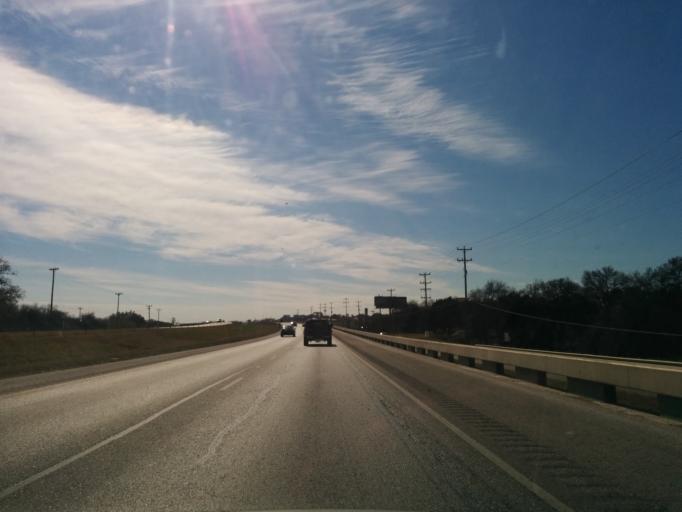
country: US
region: Texas
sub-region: Bexar County
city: Cross Mountain
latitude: 29.6522
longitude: -98.6246
